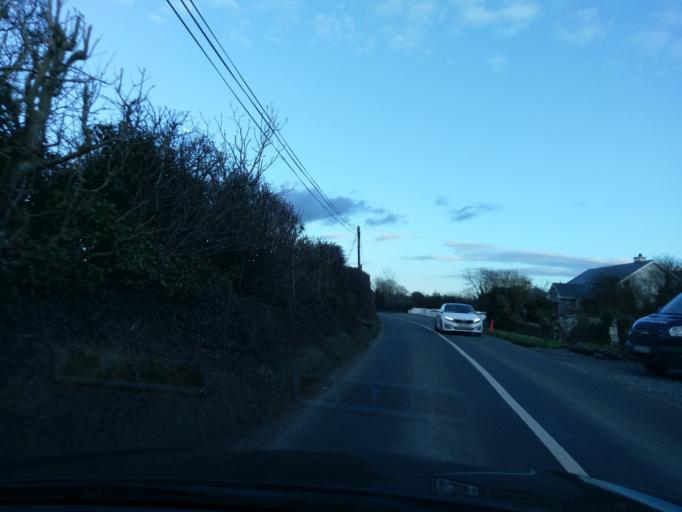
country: IE
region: Connaught
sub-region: County Galway
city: Athenry
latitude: 53.4326
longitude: -8.7109
